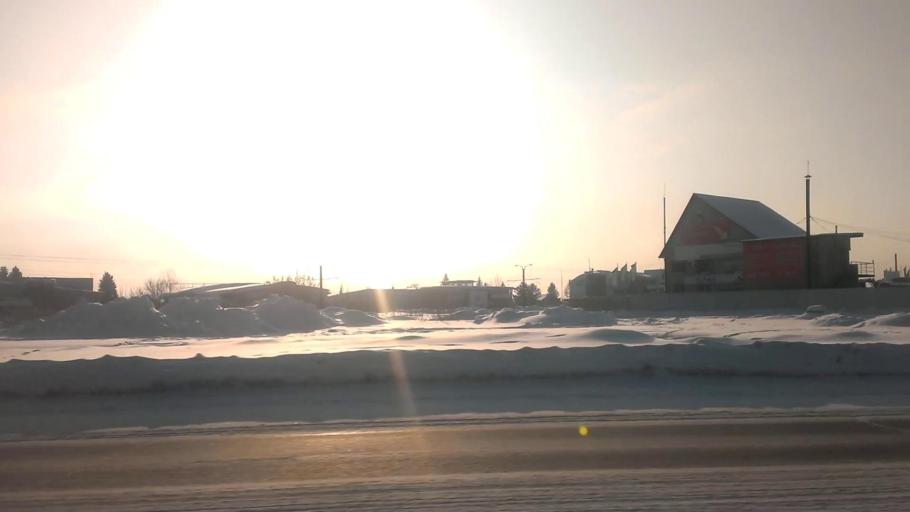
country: RU
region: Altai Krai
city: Novosilikatnyy
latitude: 53.3304
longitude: 83.6613
